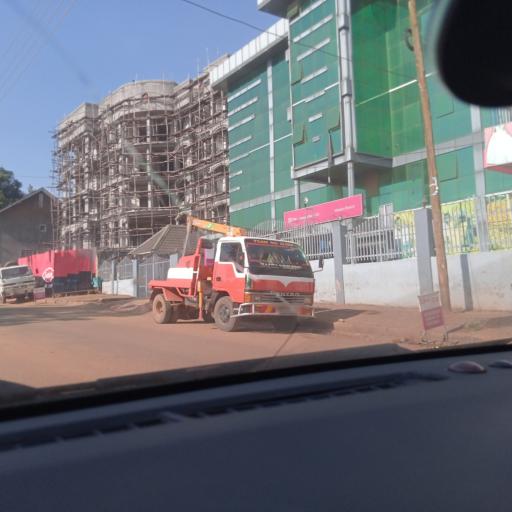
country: UG
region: Central Region
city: Masaka
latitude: -0.3448
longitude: 31.7369
